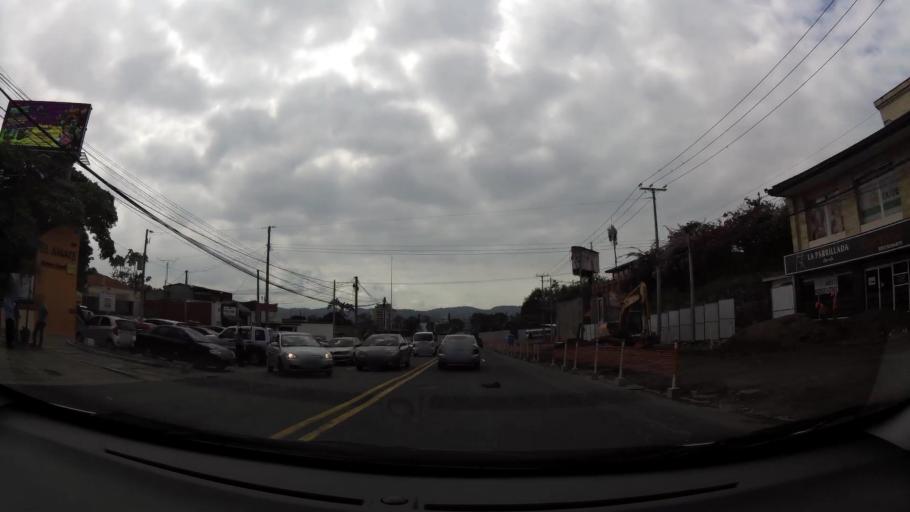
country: SV
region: La Libertad
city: Antiguo Cuscatlan
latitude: 13.7050
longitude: -89.2493
